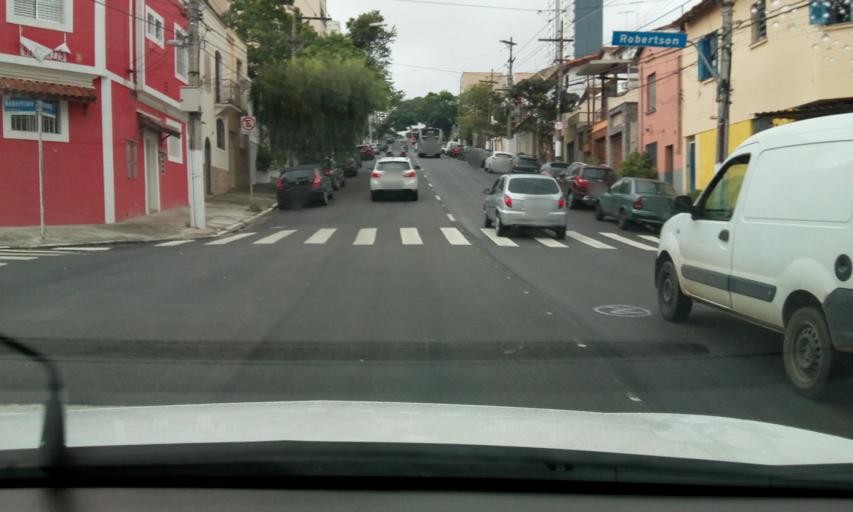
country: BR
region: Sao Paulo
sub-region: Sao Paulo
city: Sao Paulo
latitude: -23.5732
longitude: -46.6245
